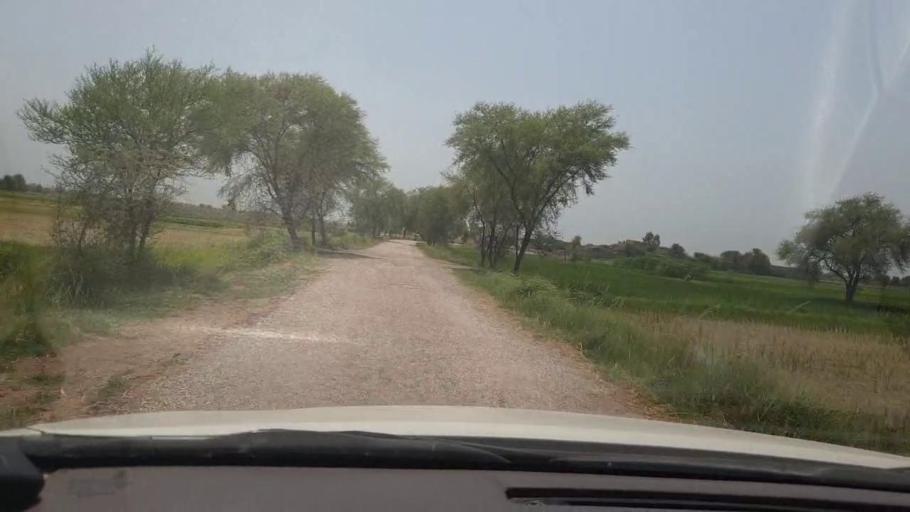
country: PK
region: Sindh
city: Garhi Yasin
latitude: 27.9103
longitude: 68.5541
